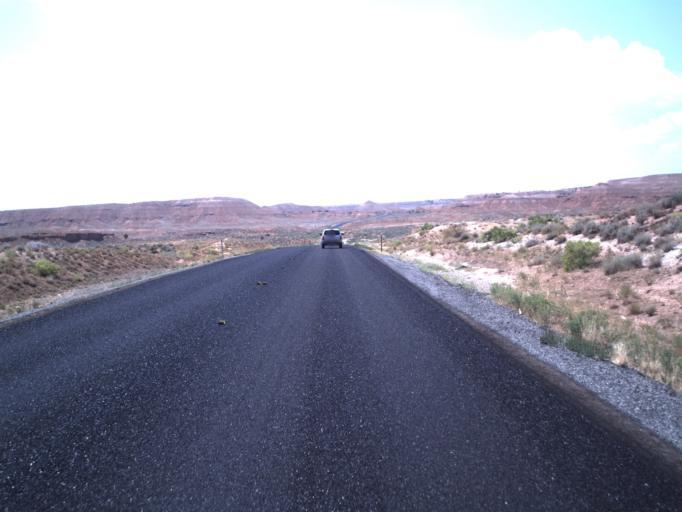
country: US
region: Utah
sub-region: Uintah County
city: Maeser
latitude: 40.4107
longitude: -109.7168
